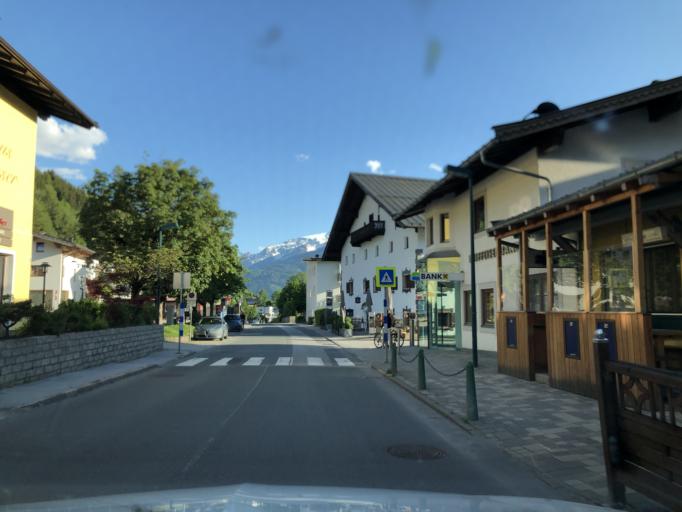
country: AT
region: Salzburg
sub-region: Politischer Bezirk Zell am See
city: Zell am See
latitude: 47.3295
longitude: 12.8169
